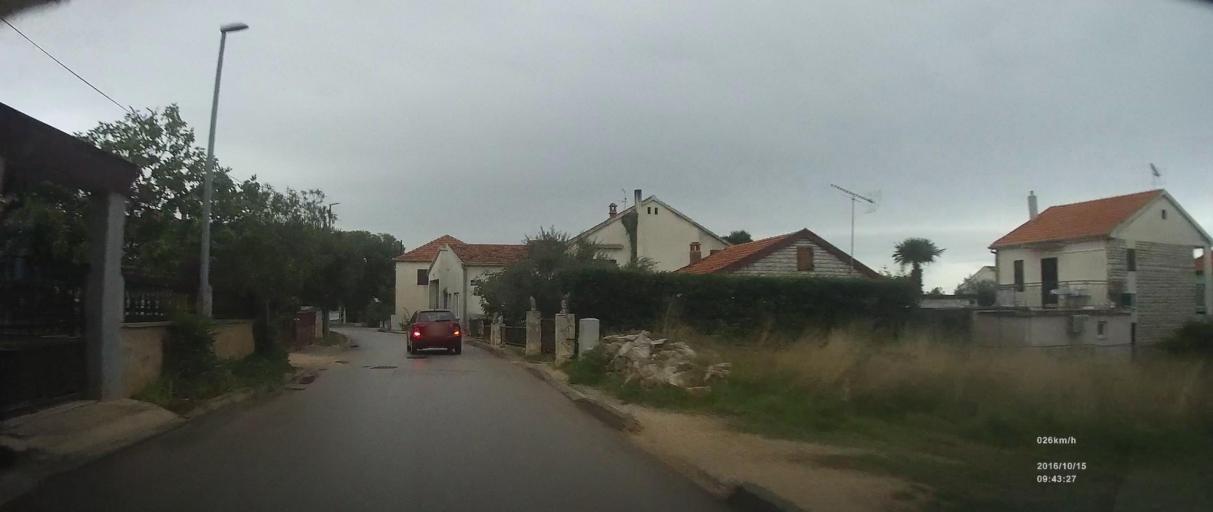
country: HR
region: Zadarska
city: Pakostane
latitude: 43.9110
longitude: 15.5046
